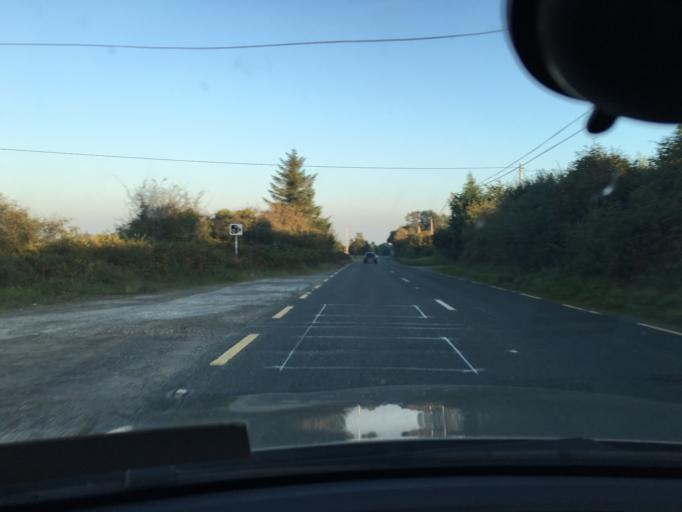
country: IE
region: Connaught
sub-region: County Galway
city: Moycullen
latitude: 53.3719
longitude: -9.2365
